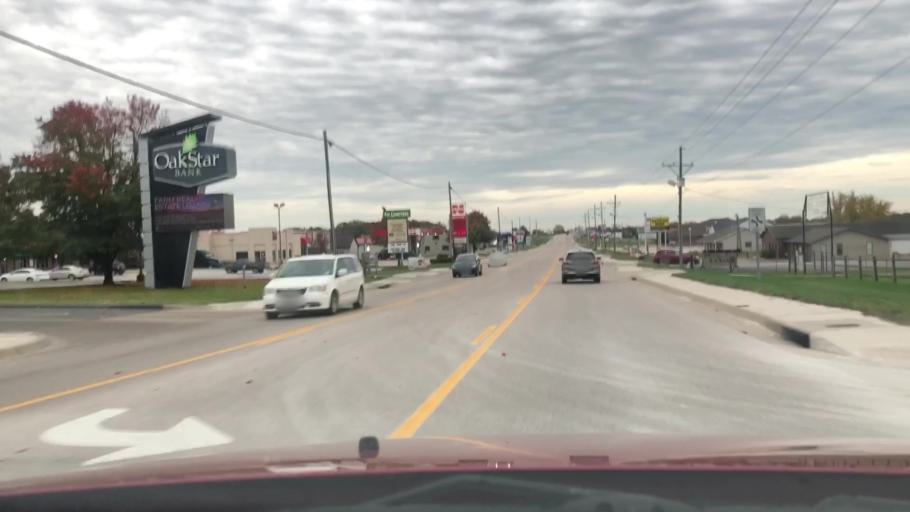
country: US
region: Missouri
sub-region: Dallas County
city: Buffalo
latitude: 37.6338
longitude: -93.1046
